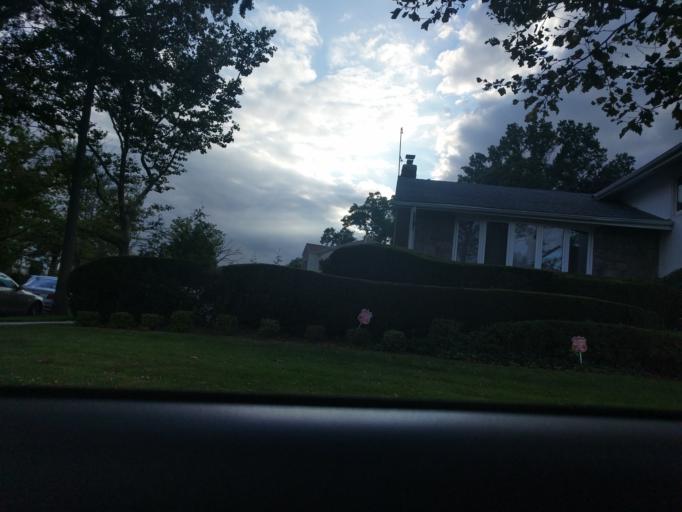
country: US
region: New York
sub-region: Nassau County
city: South Valley Stream
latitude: 40.6489
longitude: -73.7241
